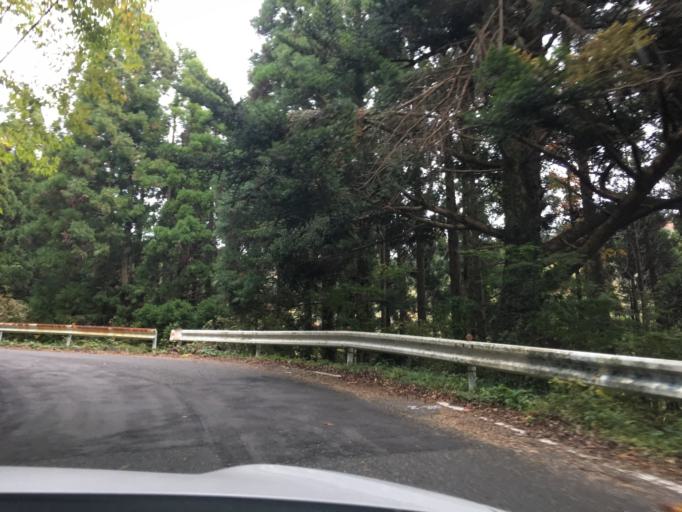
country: JP
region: Fukushima
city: Iwaki
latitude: 37.0958
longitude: 140.7983
